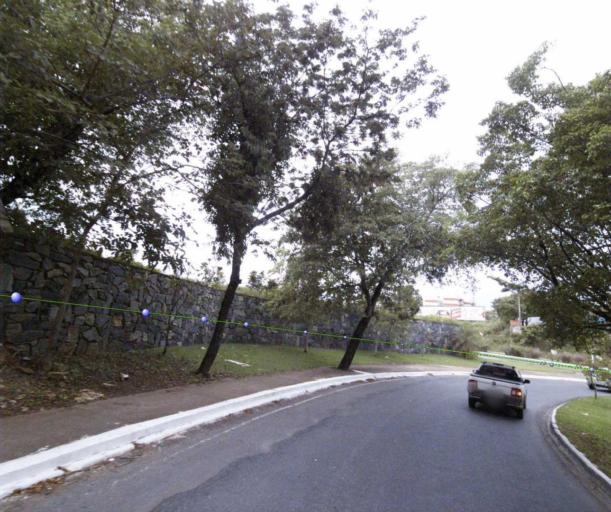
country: BR
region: Mato Grosso
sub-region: Cuiaba
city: Cuiaba
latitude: -15.6078
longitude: -56.0818
